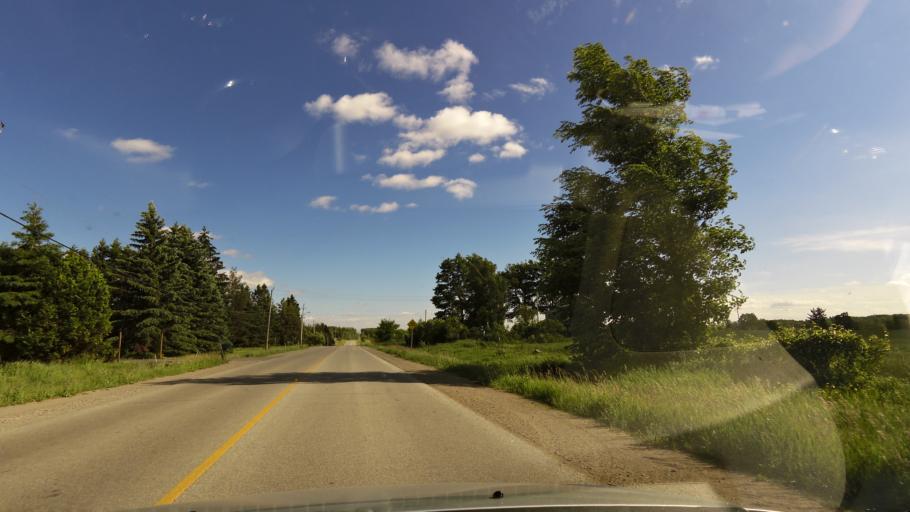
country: CA
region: Ontario
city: Bradford West Gwillimbury
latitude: 44.1439
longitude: -79.6112
